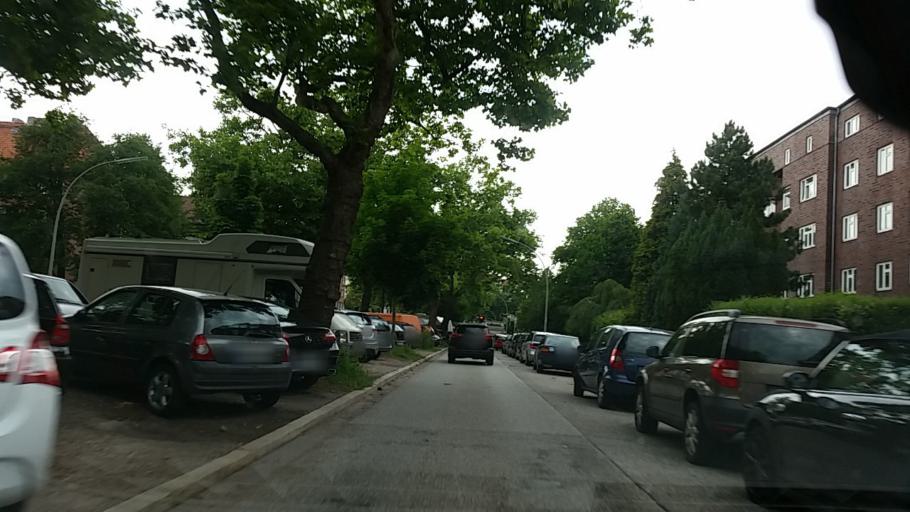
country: DE
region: Hamburg
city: Altona
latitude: 53.5552
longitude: 9.9182
